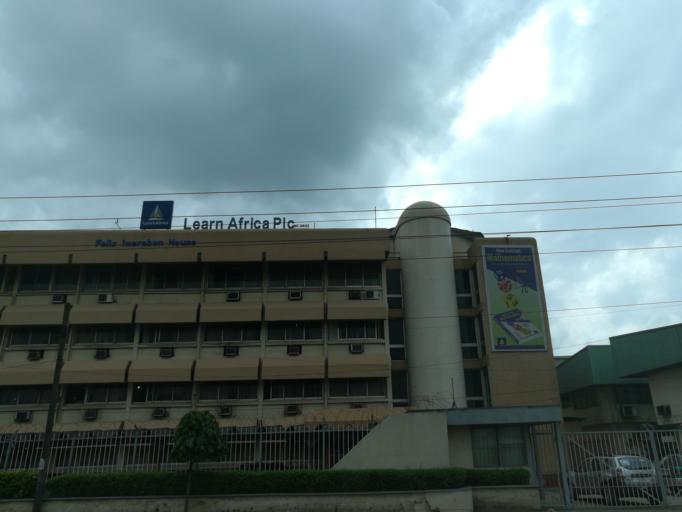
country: NG
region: Lagos
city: Ikeja
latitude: 6.6023
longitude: 3.3380
